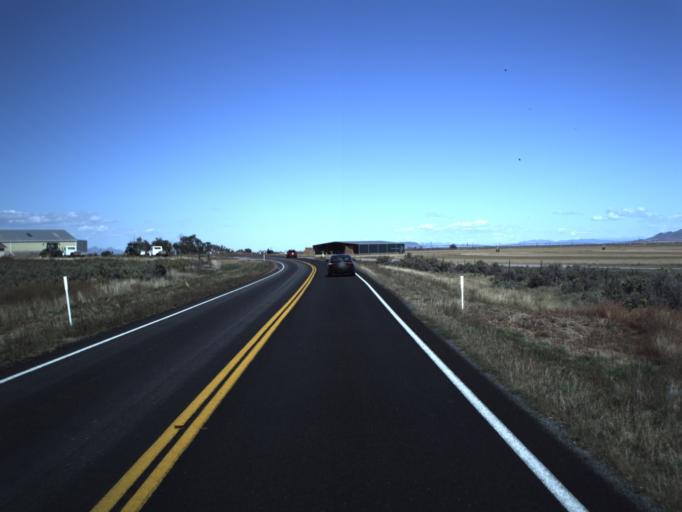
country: US
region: Utah
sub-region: Washington County
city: Enterprise
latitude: 37.6737
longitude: -113.6589
